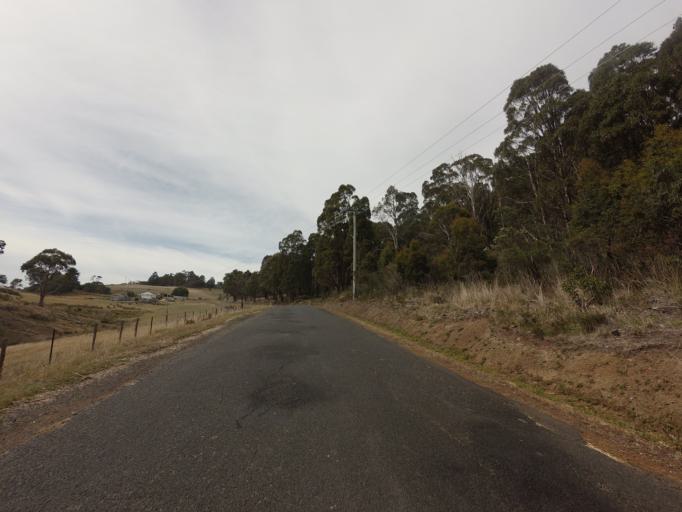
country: AU
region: Tasmania
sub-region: Sorell
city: Sorell
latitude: -42.4431
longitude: 147.5390
